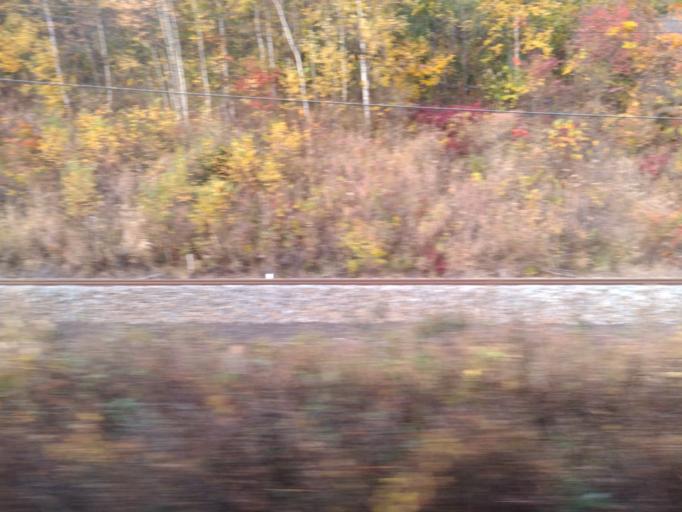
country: JP
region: Hokkaido
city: Niseko Town
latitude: 42.5877
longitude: 140.6990
